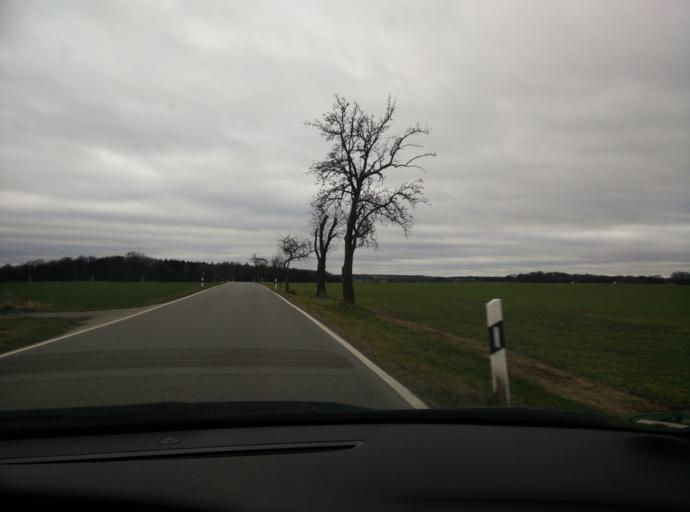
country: DE
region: Saxony
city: Geithain
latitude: 51.0266
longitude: 12.6801
